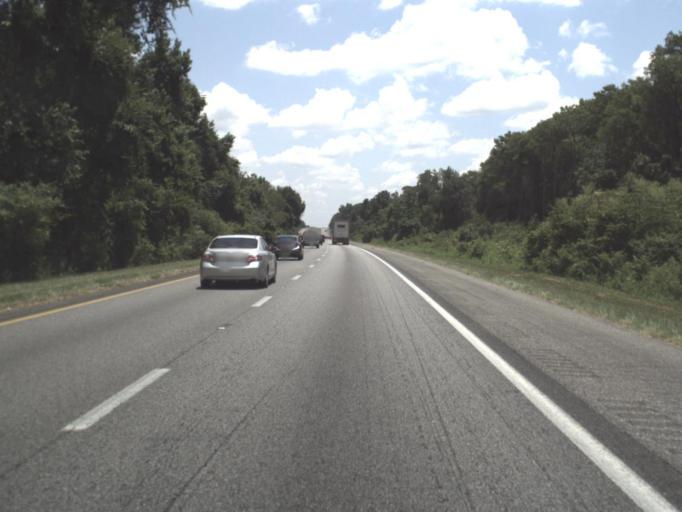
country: US
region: Florida
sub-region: Madison County
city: Madison
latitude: 30.4303
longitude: -83.5577
